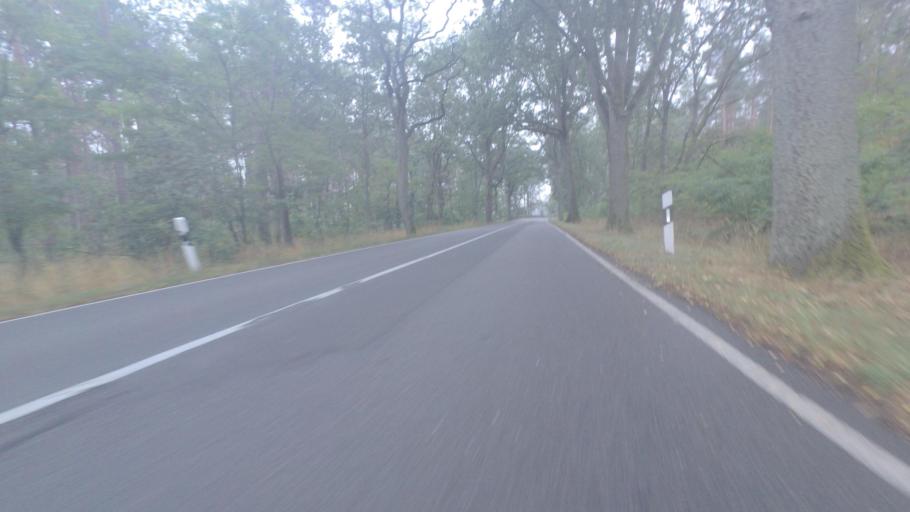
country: DE
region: Brandenburg
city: Heiligengrabe
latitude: 53.0972
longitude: 12.3649
